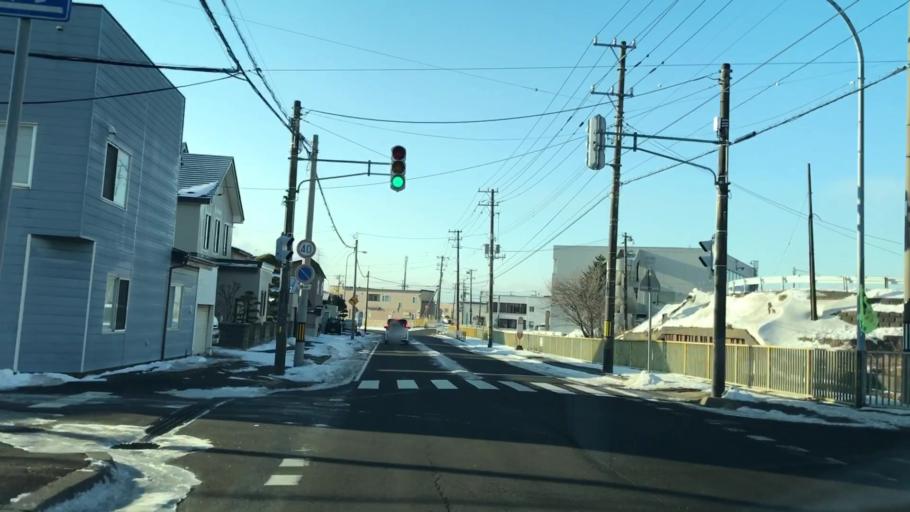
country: JP
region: Hokkaido
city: Muroran
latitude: 42.3664
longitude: 141.0492
